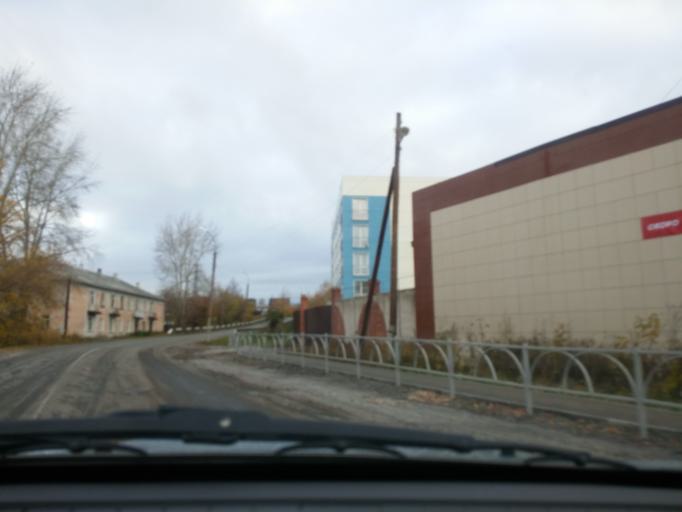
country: RU
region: Sverdlovsk
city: Turinsk
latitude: 58.0410
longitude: 63.7071
